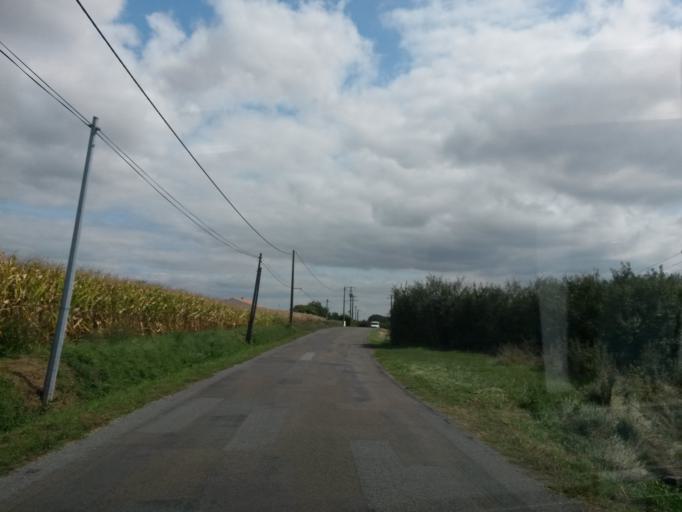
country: FR
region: Pays de la Loire
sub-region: Departement de la Vendee
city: Jard-sur-Mer
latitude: 46.4344
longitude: -1.5889
